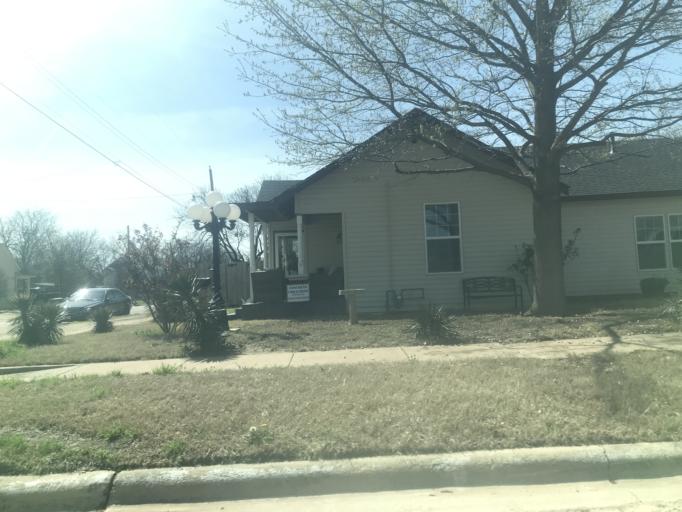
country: US
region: Texas
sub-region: Taylor County
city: Abilene
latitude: 32.4690
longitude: -99.7368
